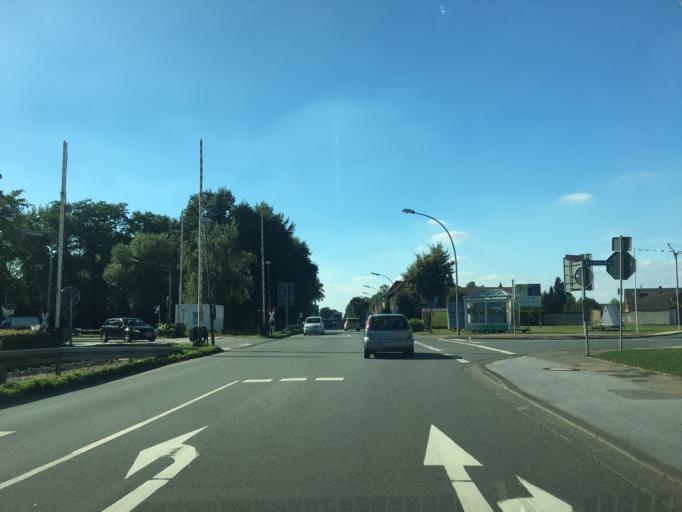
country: DE
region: North Rhine-Westphalia
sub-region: Regierungsbezirk Munster
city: Beelen
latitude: 51.9028
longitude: 8.1921
